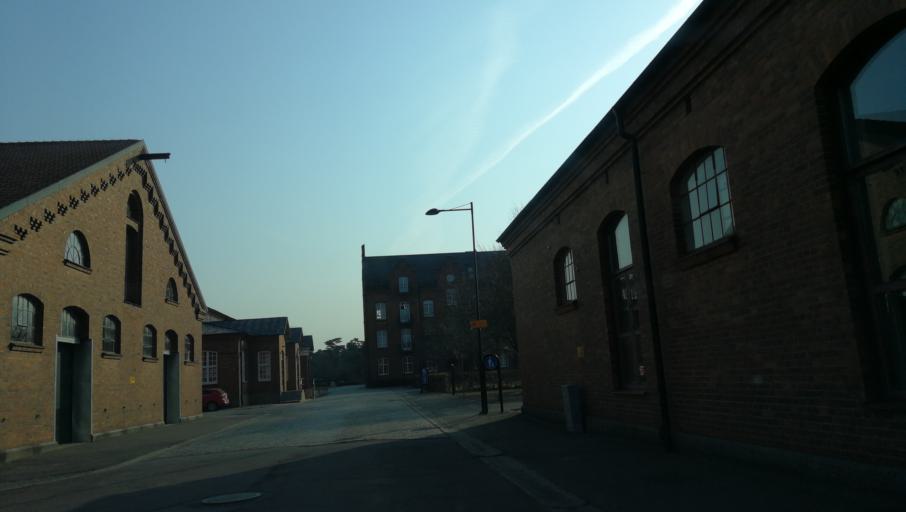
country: SE
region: Skane
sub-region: Ystads Kommun
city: Ystad
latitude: 55.4320
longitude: 13.8424
